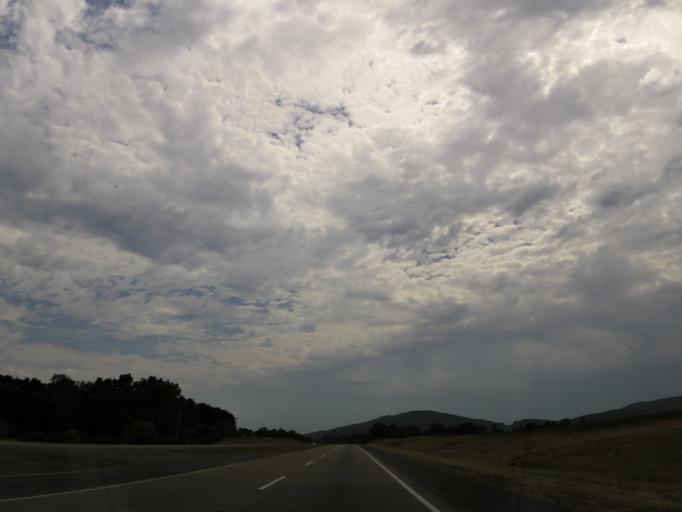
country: US
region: Alabama
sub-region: Jackson County
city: Stevenson
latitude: 34.9068
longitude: -85.7993
